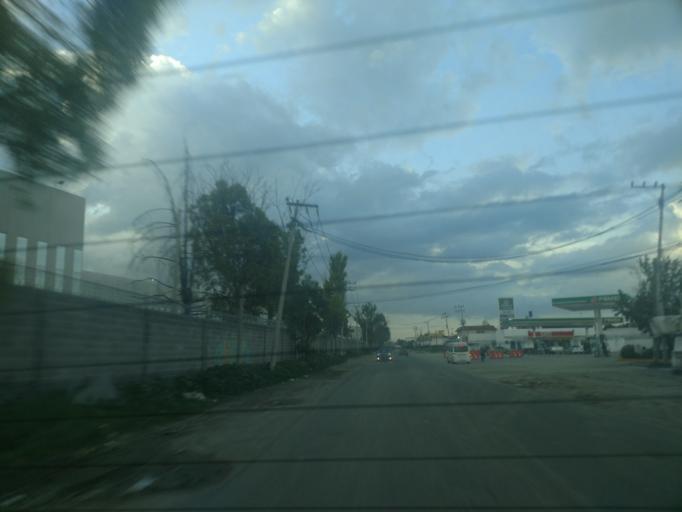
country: MX
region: Mexico
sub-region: Cuautitlan
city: Barrio Tlatenco
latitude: 19.7423
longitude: -99.1994
